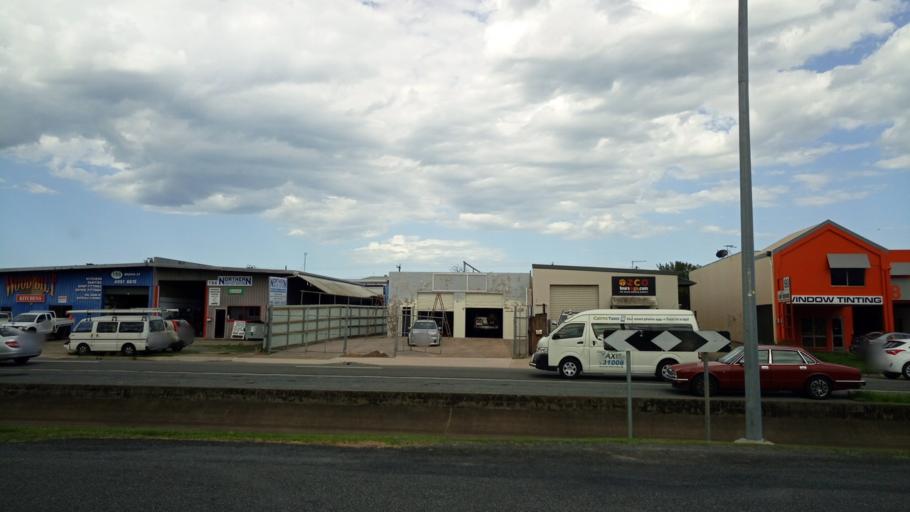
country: AU
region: Queensland
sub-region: Cairns
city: Woree
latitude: -16.9361
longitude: 145.7563
